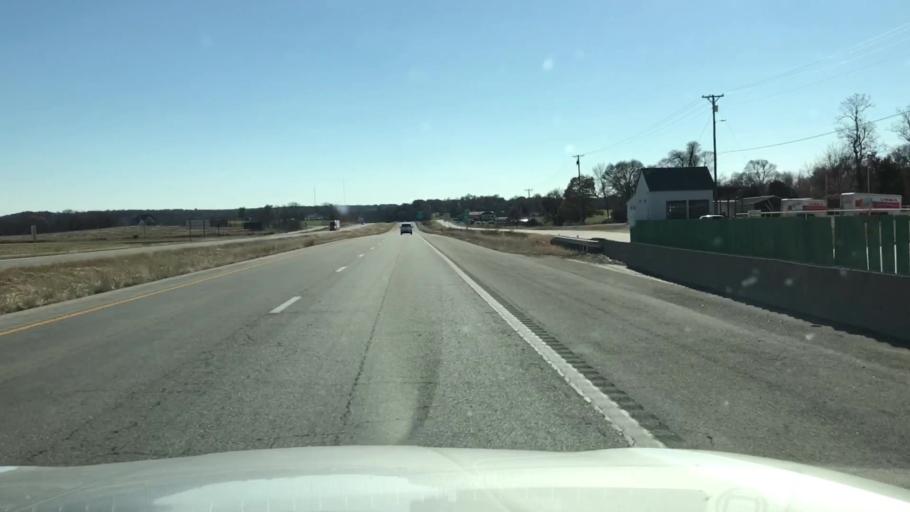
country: US
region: Missouri
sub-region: Jasper County
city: Carthage
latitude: 37.1223
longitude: -94.3112
